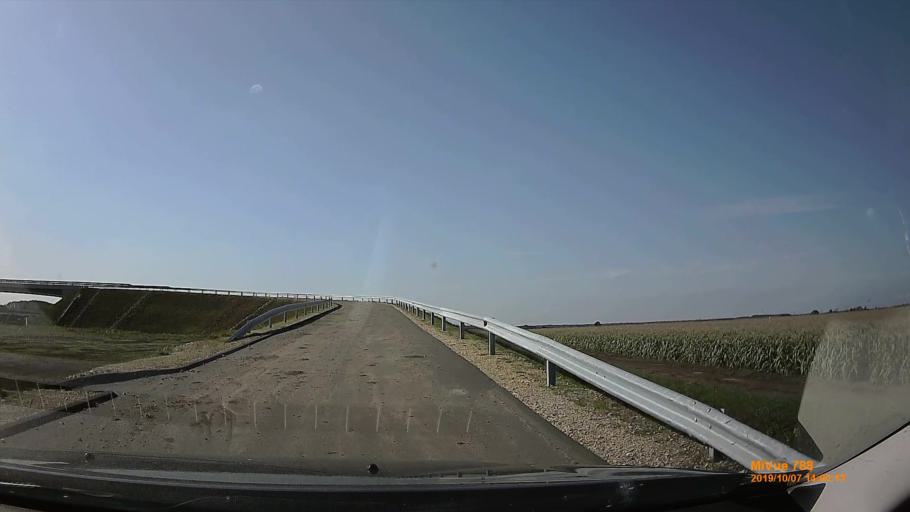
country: HU
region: Jasz-Nagykun-Szolnok
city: Cserkeszolo
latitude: 46.8850
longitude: 20.2136
